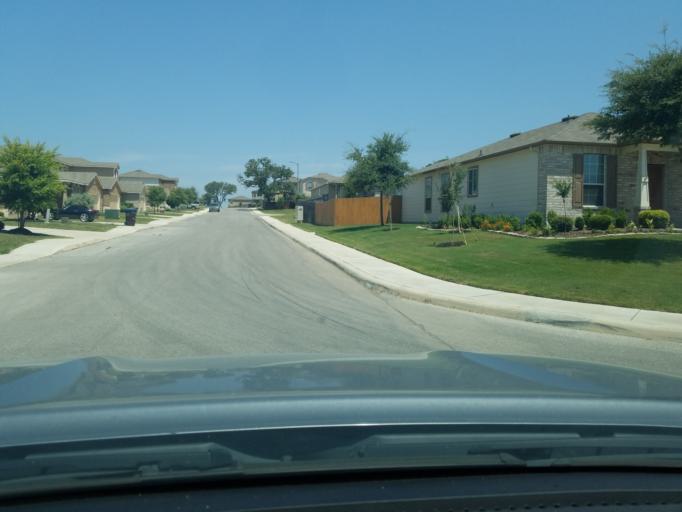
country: US
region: Texas
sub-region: Bexar County
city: Timberwood Park
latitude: 29.7050
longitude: -98.4818
